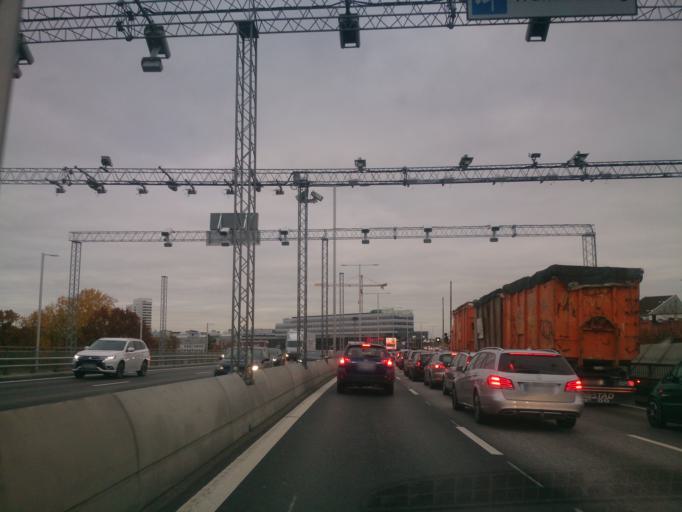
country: SE
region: Stockholm
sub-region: Solna Kommun
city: Solna
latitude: 59.3335
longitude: 18.0093
